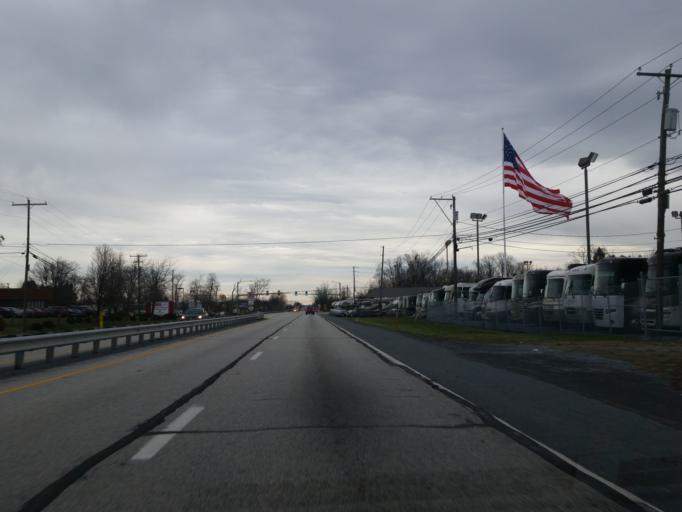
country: US
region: Pennsylvania
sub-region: Dauphin County
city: Skyline View
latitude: 40.3344
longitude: -76.7329
